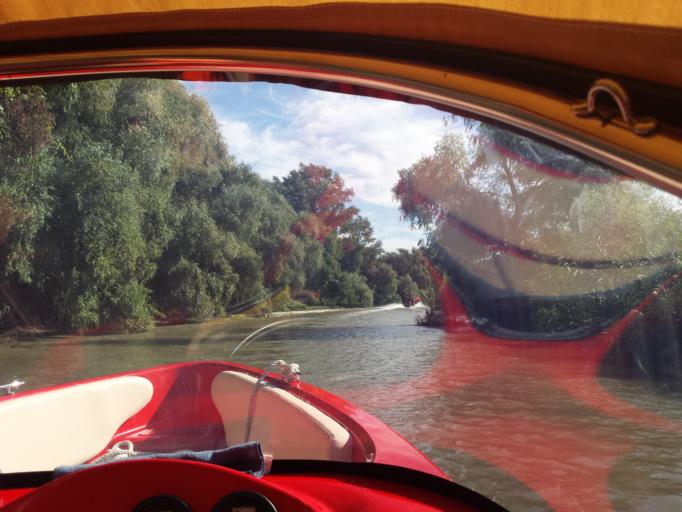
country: RO
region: Tulcea
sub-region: Comuna Pardina
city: Pardina
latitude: 45.2456
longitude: 29.0248
